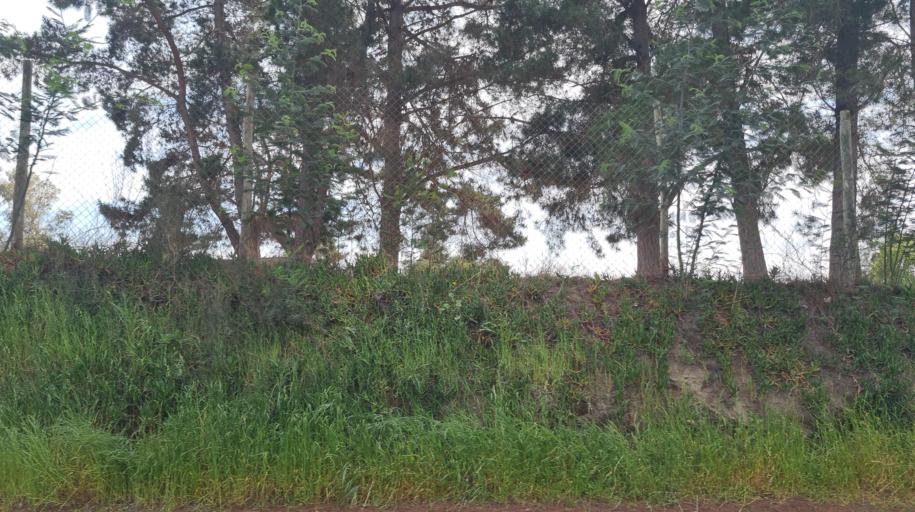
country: CL
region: O'Higgins
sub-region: Provincia de Cachapoal
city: San Vicente
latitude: -34.1505
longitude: -71.4576
